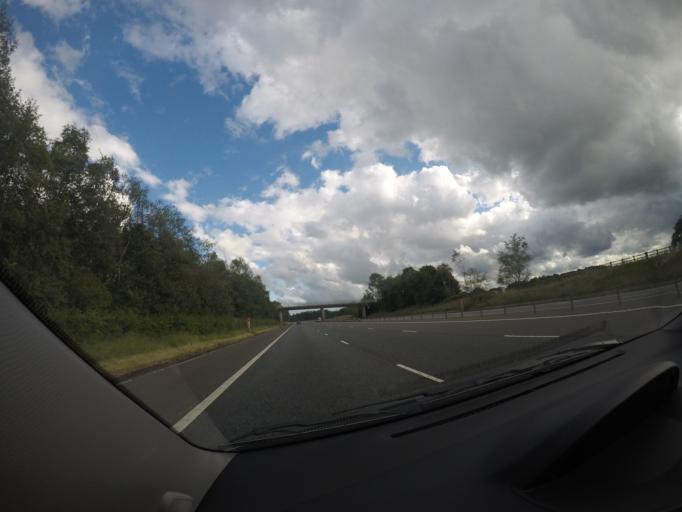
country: GB
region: Scotland
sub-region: Dumfries and Galloway
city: Lochmaben
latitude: 55.1836
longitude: -3.4058
